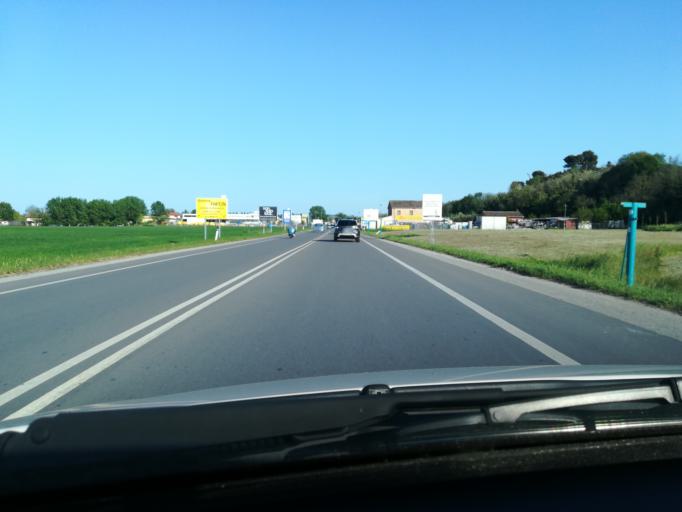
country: IT
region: Emilia-Romagna
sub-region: Provincia di Rimini
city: Misano Adriatico
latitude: 43.9728
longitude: 12.6982
